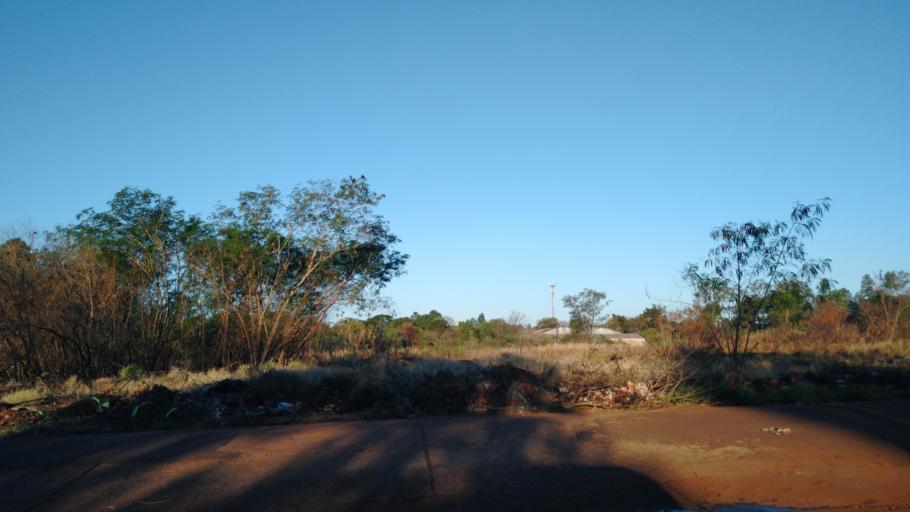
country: AR
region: Misiones
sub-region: Departamento de Capital
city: Posadas
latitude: -27.4056
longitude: -55.9493
